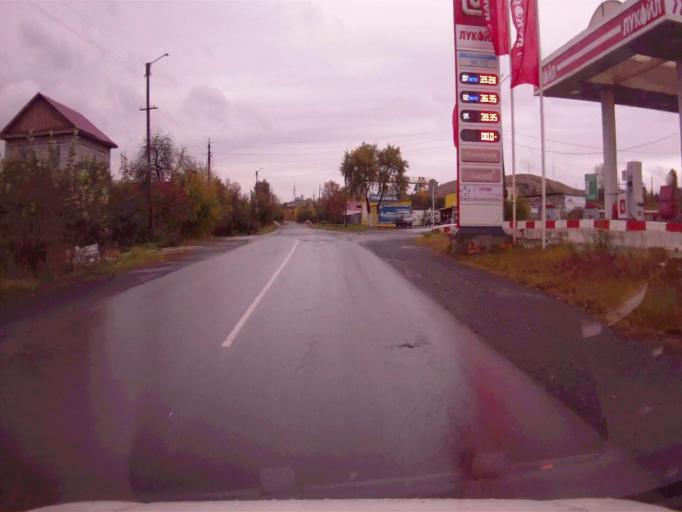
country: RU
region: Chelyabinsk
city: Verkhniy Ufaley
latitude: 56.0507
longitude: 60.2453
